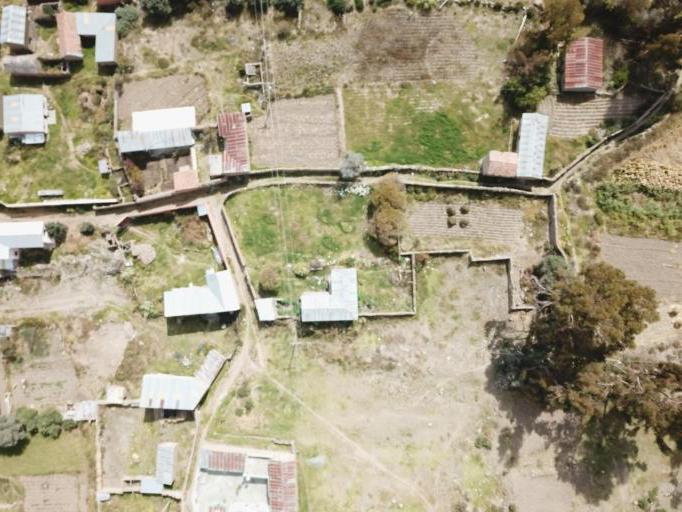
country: BO
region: La Paz
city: Achacachi
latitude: -16.0525
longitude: -68.8134
